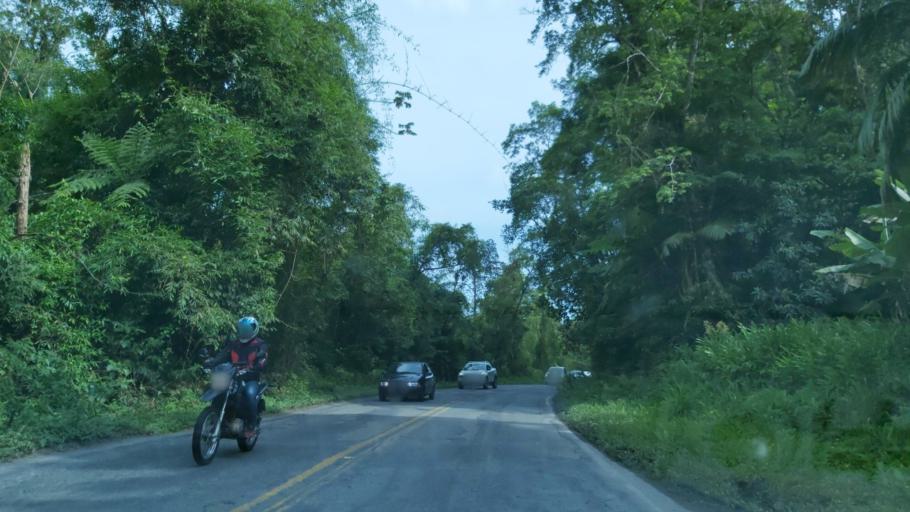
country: BR
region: Sao Paulo
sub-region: Miracatu
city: Miracatu
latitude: -24.0498
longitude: -47.5707
